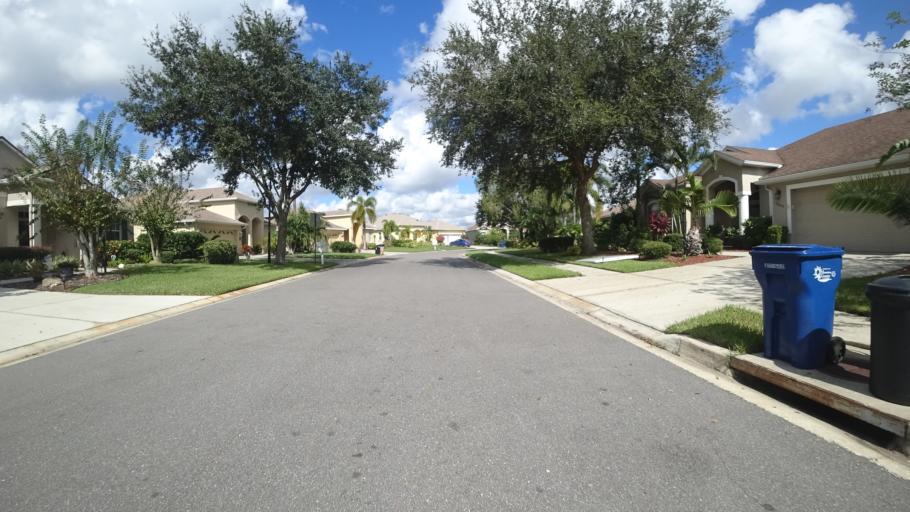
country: US
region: Florida
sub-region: Manatee County
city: Ellenton
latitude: 27.4956
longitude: -82.4419
